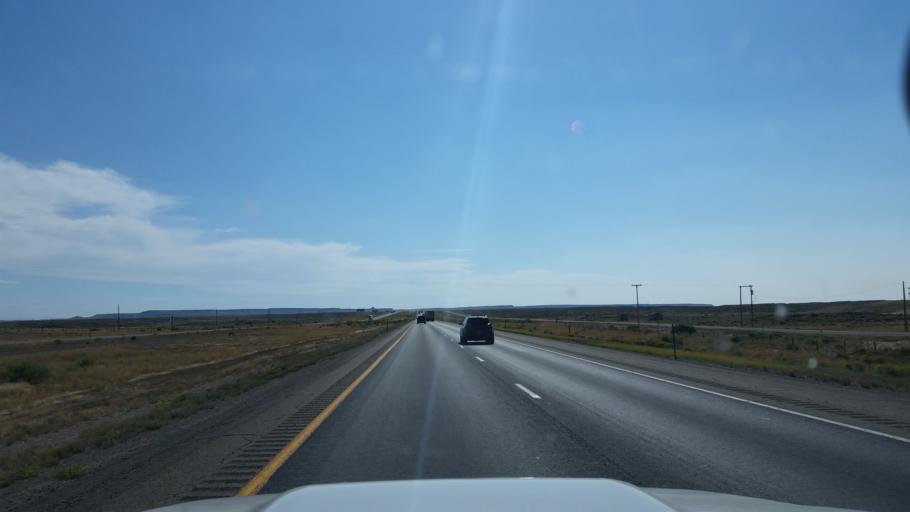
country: US
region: Wyoming
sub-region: Uinta County
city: Lyman
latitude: 41.5326
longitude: -109.9397
